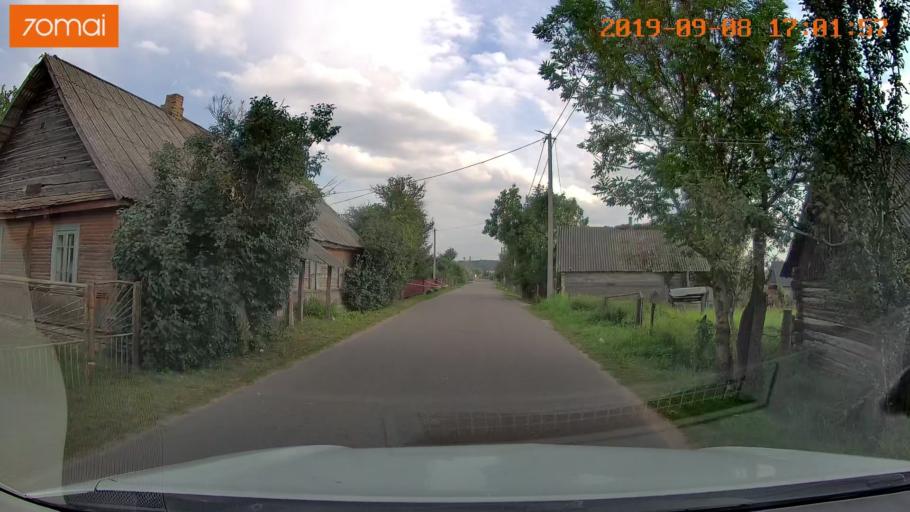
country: BY
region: Grodnenskaya
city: Hrodna
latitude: 53.7064
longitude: 23.9367
